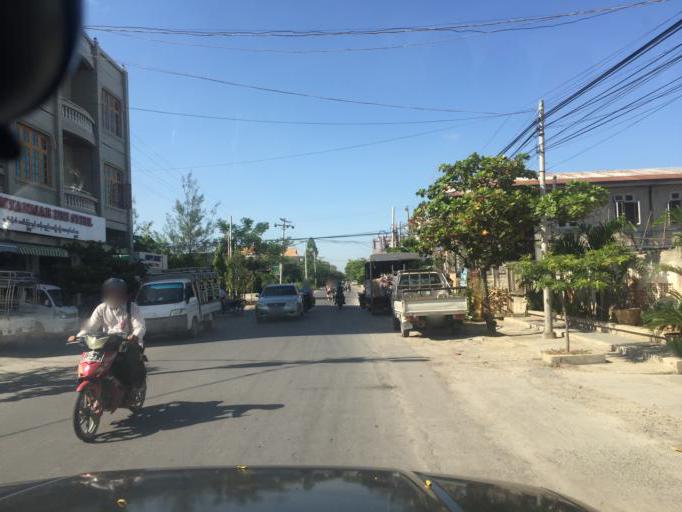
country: MM
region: Mandalay
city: Mandalay
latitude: 21.9554
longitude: 96.1099
